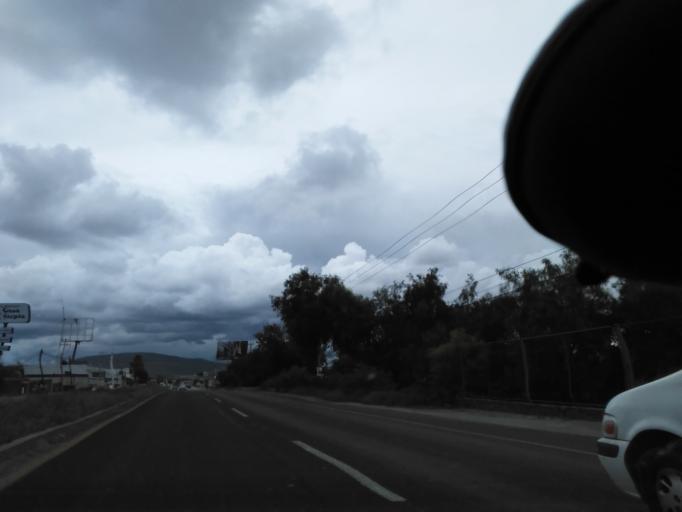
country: MX
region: Hidalgo
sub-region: Tula de Allende
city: Residencial Arboledas
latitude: 20.0582
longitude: -99.2939
